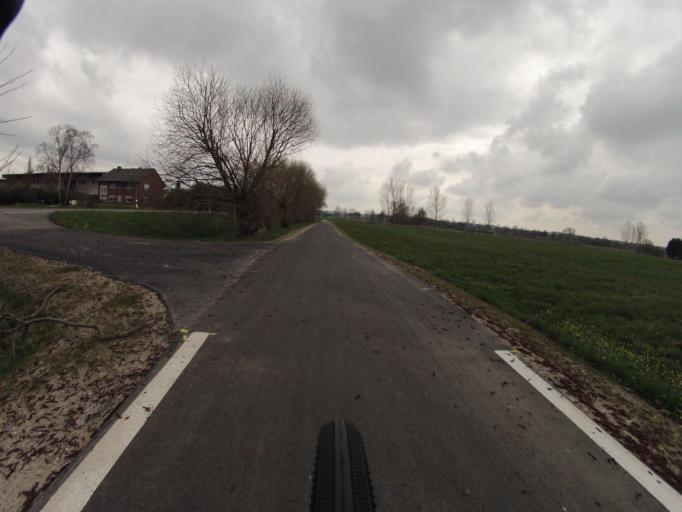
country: DE
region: North Rhine-Westphalia
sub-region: Regierungsbezirk Munster
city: Mettingen
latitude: 52.3395
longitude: 7.7801
